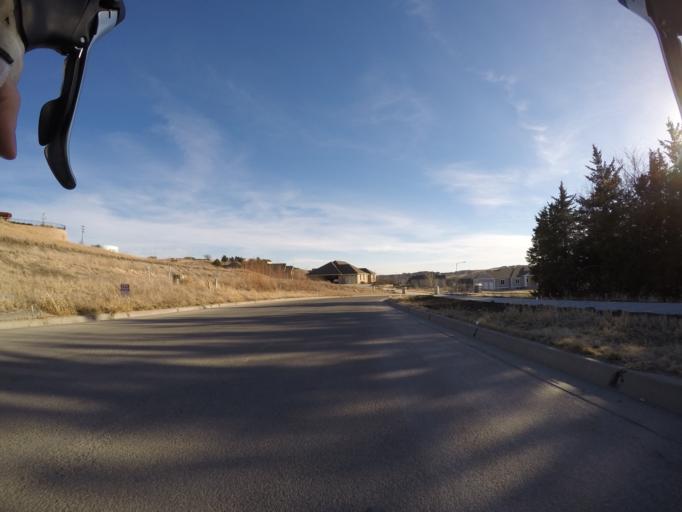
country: US
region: Kansas
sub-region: Riley County
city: Manhattan
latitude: 39.2120
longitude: -96.6315
